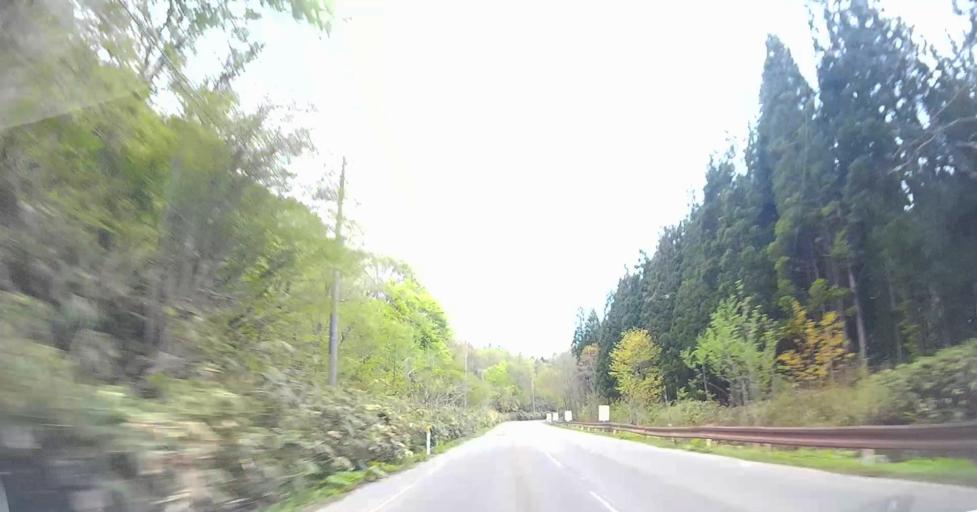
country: JP
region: Aomori
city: Goshogawara
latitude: 41.1161
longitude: 140.5274
